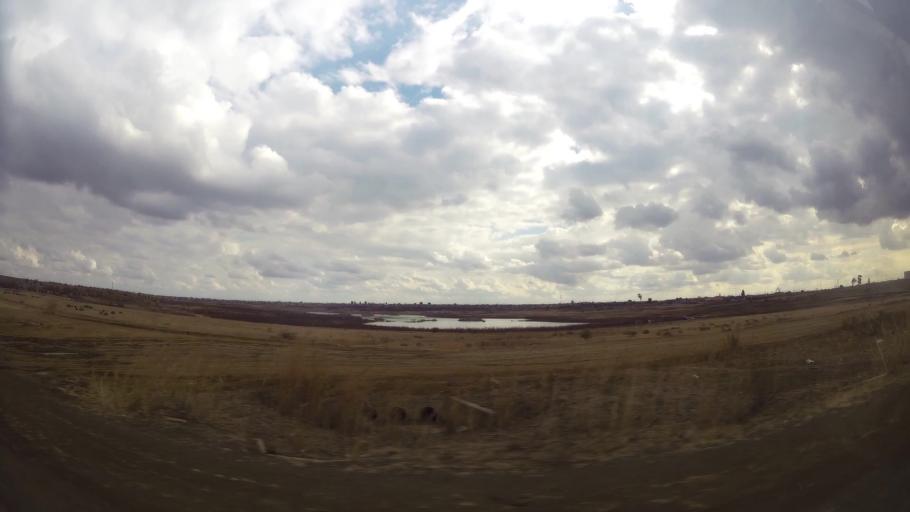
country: ZA
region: Orange Free State
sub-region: Fezile Dabi District Municipality
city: Sasolburg
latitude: -26.8676
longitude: 27.8876
